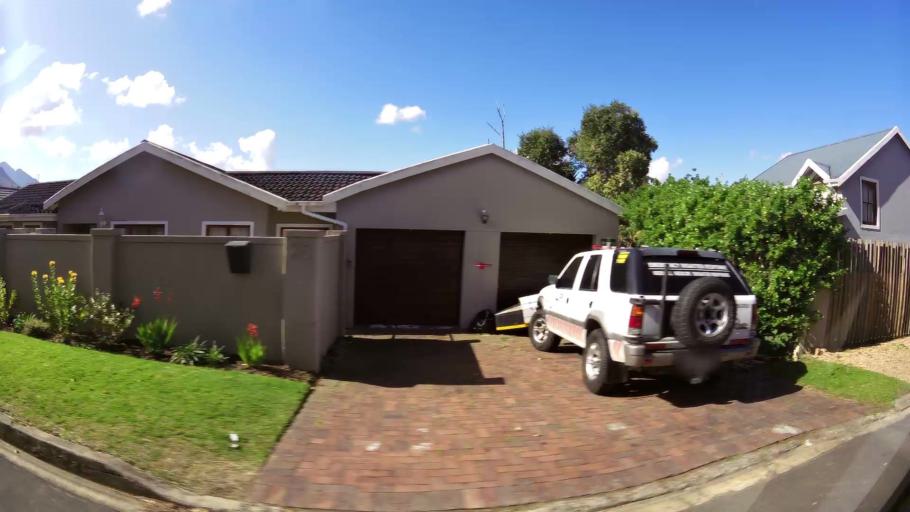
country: ZA
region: Western Cape
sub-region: Eden District Municipality
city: George
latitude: -33.9485
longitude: 22.4809
